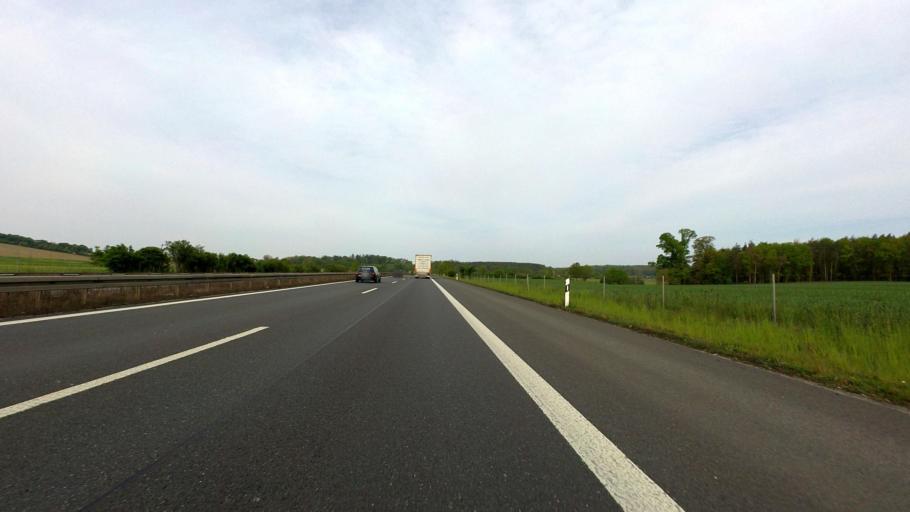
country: DE
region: Saxony
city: Wachau
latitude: 51.1714
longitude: 13.8948
